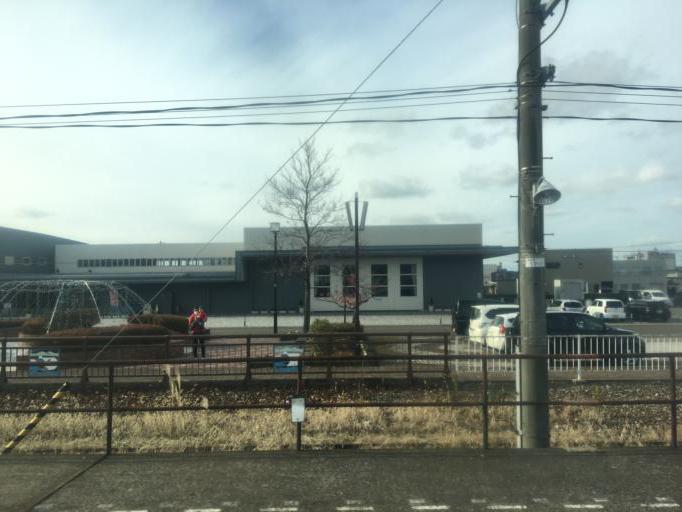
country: JP
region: Akita
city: Tenno
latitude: 39.9481
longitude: 140.0784
